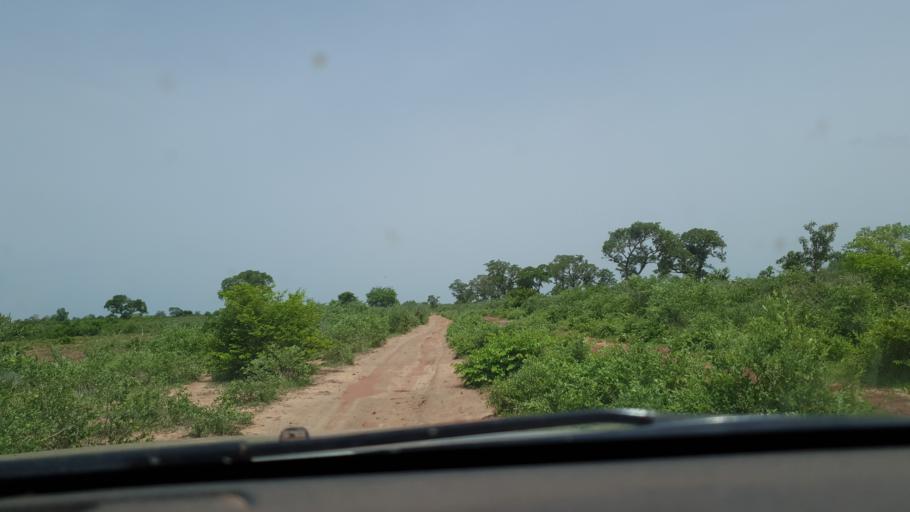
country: ML
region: Koulikoro
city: Koulikoro
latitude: 12.6649
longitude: -7.2194
